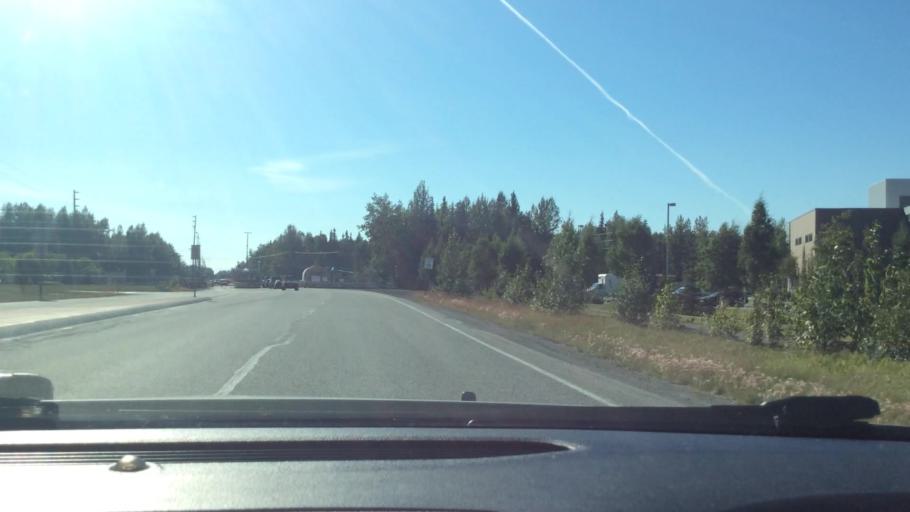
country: US
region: Alaska
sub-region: Anchorage Municipality
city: Elmendorf Air Force Base
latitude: 61.2313
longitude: -149.7437
